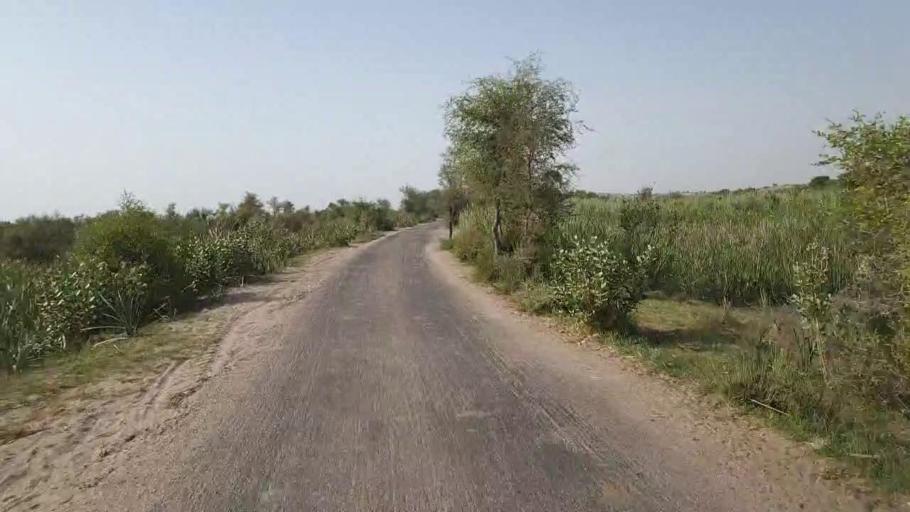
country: PK
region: Sindh
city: Kandiari
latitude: 26.7056
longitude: 68.9639
